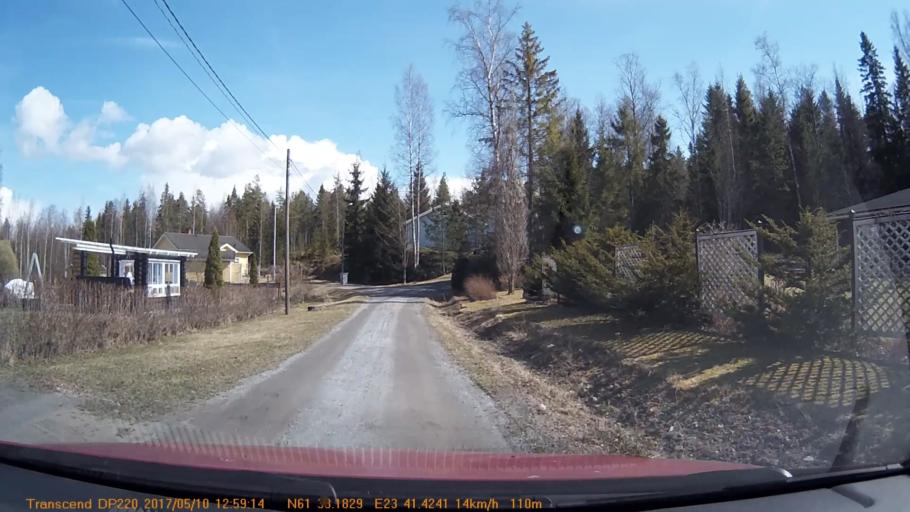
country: FI
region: Pirkanmaa
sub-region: Tampere
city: Yloejaervi
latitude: 61.5531
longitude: 23.6904
